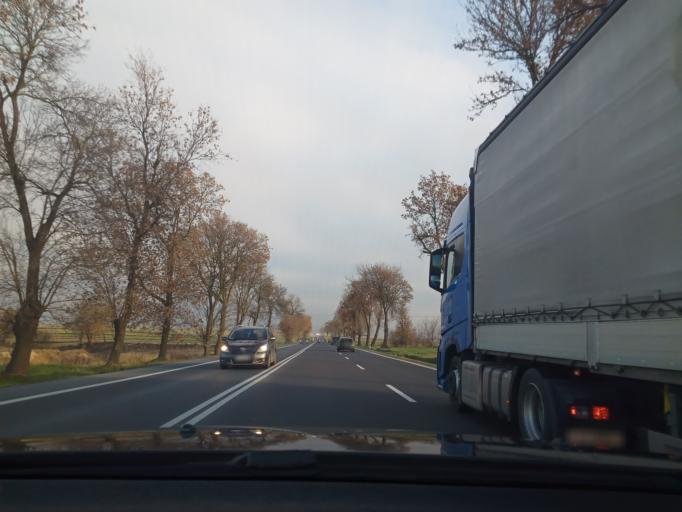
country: PL
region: Lesser Poland Voivodeship
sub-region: Powiat miechowski
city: Miechow
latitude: 50.3044
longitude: 20.0375
